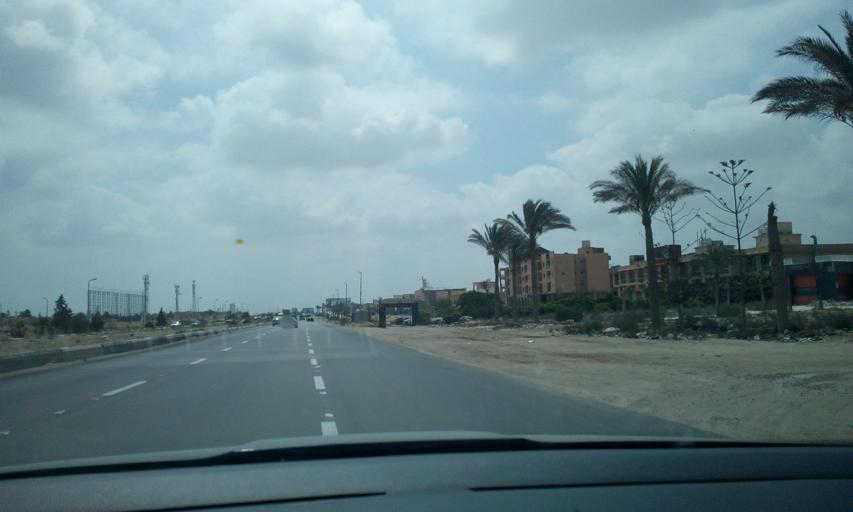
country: EG
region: Muhafazat Matruh
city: Al `Alamayn
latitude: 30.8325
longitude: 28.9651
